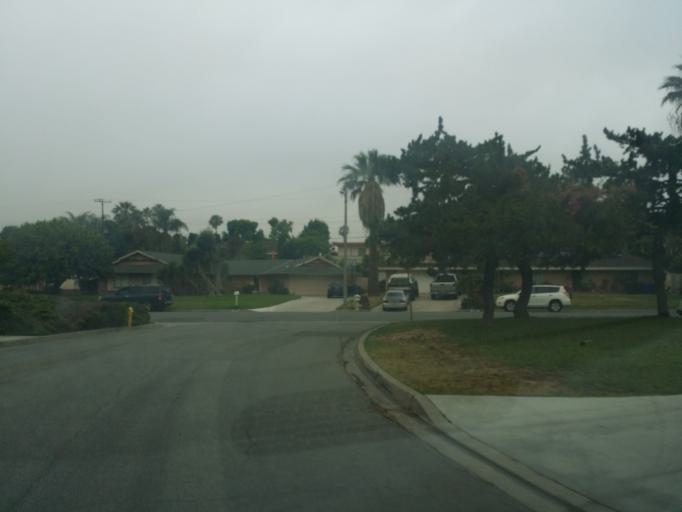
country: US
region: California
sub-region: San Bernardino County
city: Muscoy
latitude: 34.1462
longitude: -117.3787
